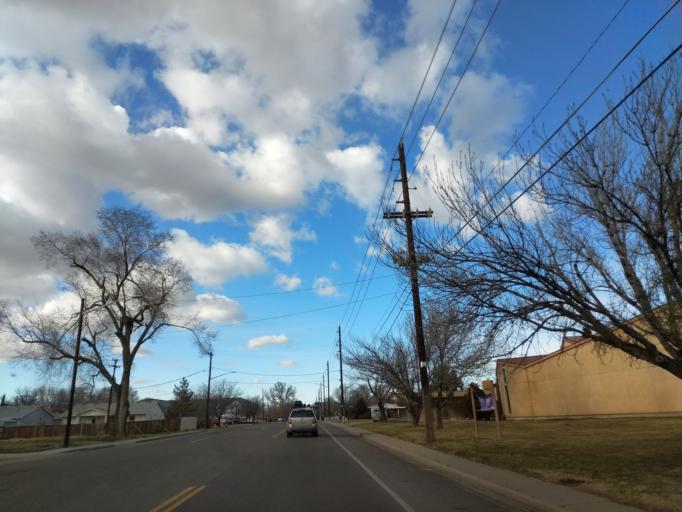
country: US
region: Colorado
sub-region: Mesa County
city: Grand Junction
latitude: 39.0789
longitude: -108.5708
